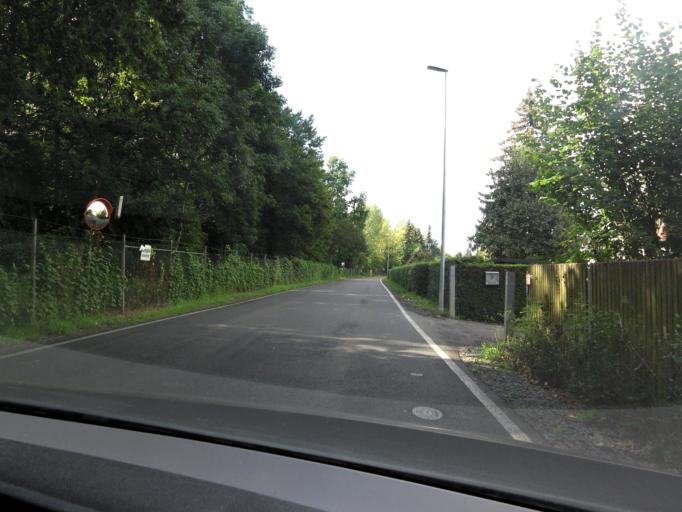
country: DE
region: Saxony
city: Taucha
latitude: 51.3721
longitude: 12.4574
